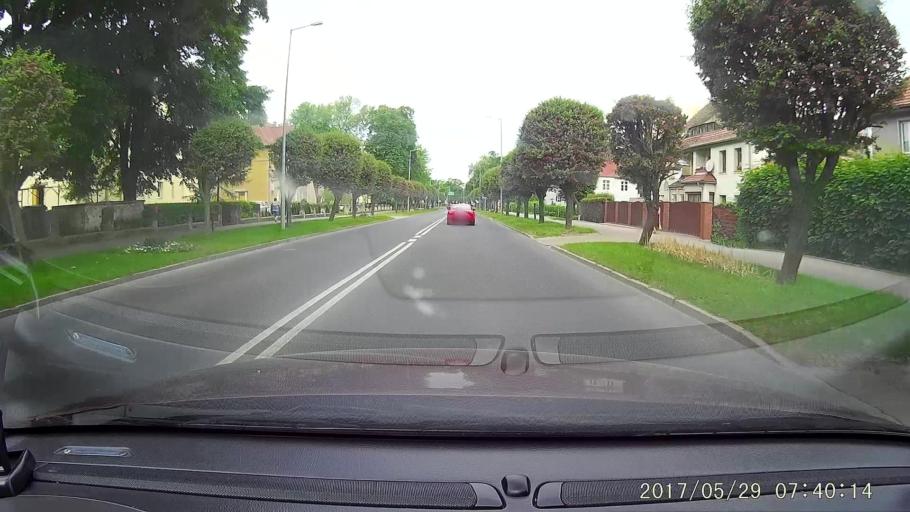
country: PL
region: Lower Silesian Voivodeship
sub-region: Powiat boleslawiecki
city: Boleslawiec
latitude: 51.2611
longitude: 15.5814
